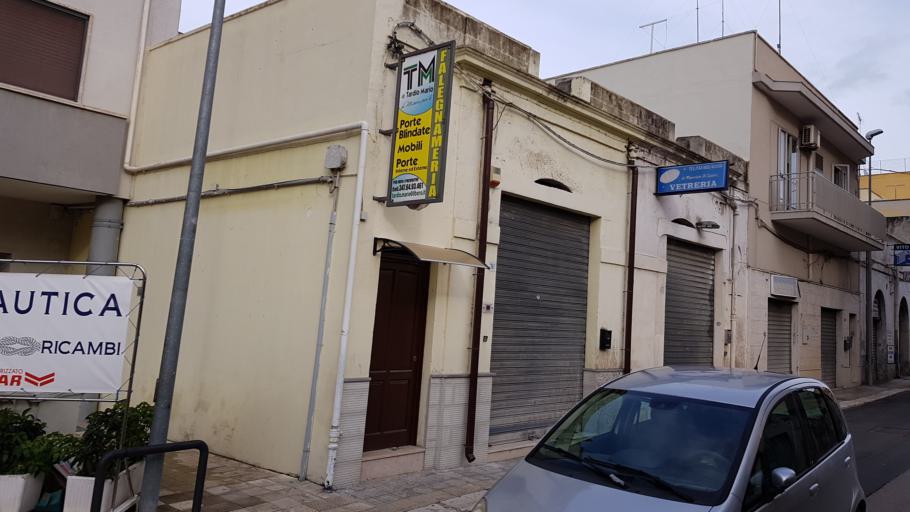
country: IT
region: Apulia
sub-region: Provincia di Brindisi
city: Brindisi
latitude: 40.6377
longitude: 17.9318
